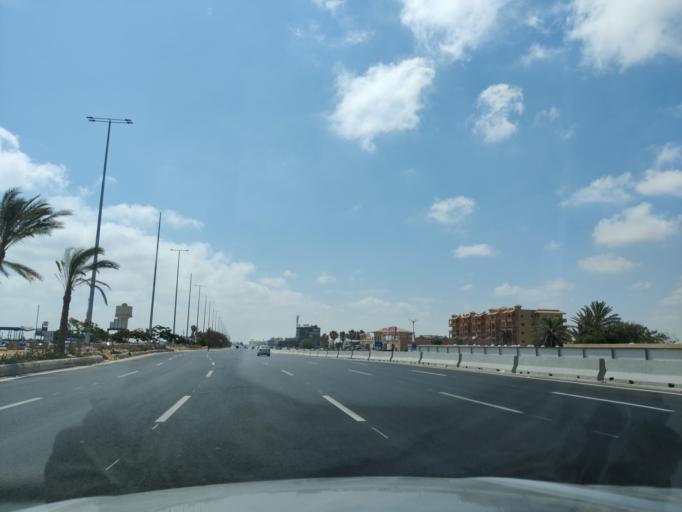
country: EG
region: Muhafazat Matruh
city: Al `Alamayn
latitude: 30.8360
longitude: 28.9582
